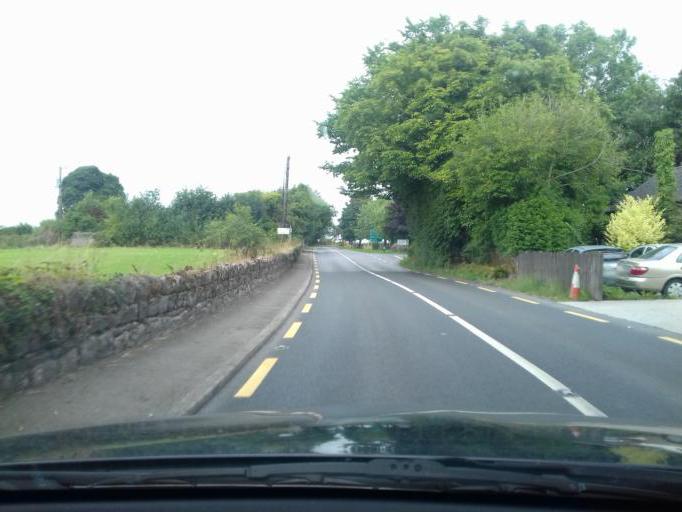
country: IE
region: Leinster
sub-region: County Carlow
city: Tullow
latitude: 52.8100
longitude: -6.7264
